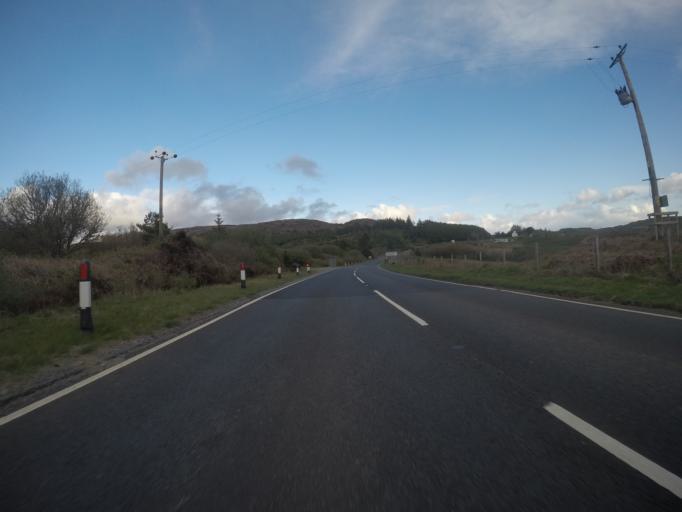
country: GB
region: Scotland
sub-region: Highland
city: Portree
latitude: 57.5317
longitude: -6.3522
